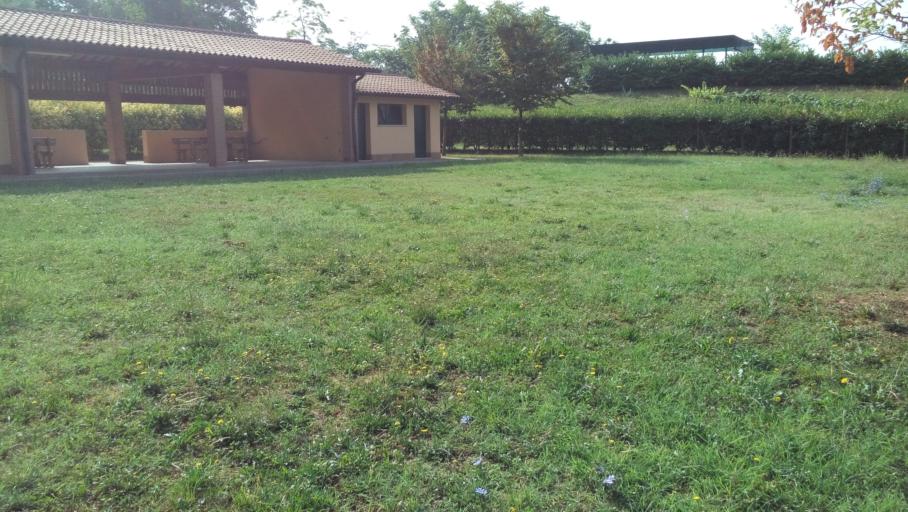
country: IT
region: Veneto
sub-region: Provincia di Vicenza
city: Creazzo
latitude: 45.5397
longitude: 11.4659
